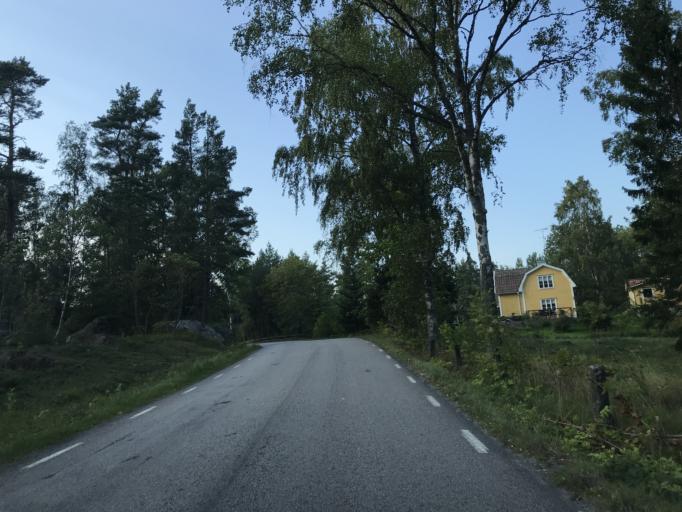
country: SE
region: Stockholm
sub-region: Norrtalje Kommun
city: Bjorko
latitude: 59.8631
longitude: 19.0361
